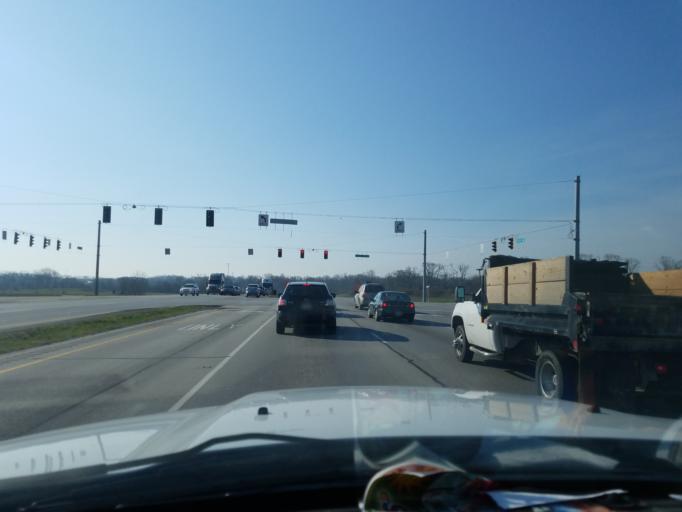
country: US
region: Indiana
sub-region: Monroe County
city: Bloomington
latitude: 39.1942
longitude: -86.5717
